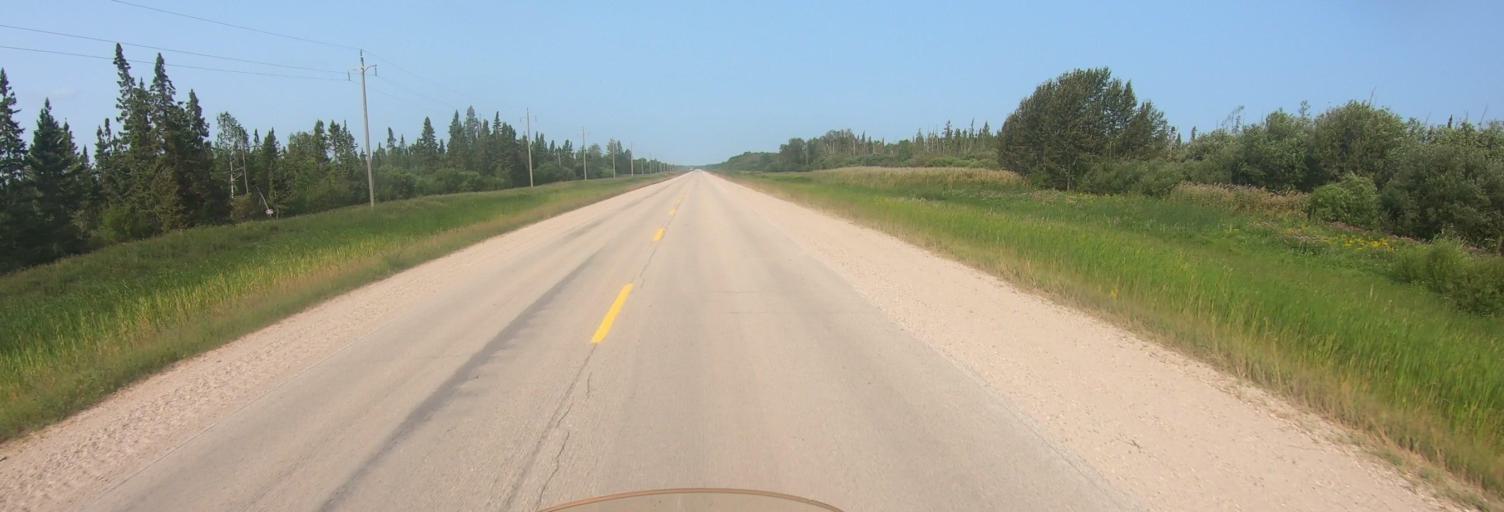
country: US
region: Minnesota
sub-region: Roseau County
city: Roseau
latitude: 49.0234
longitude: -95.6717
